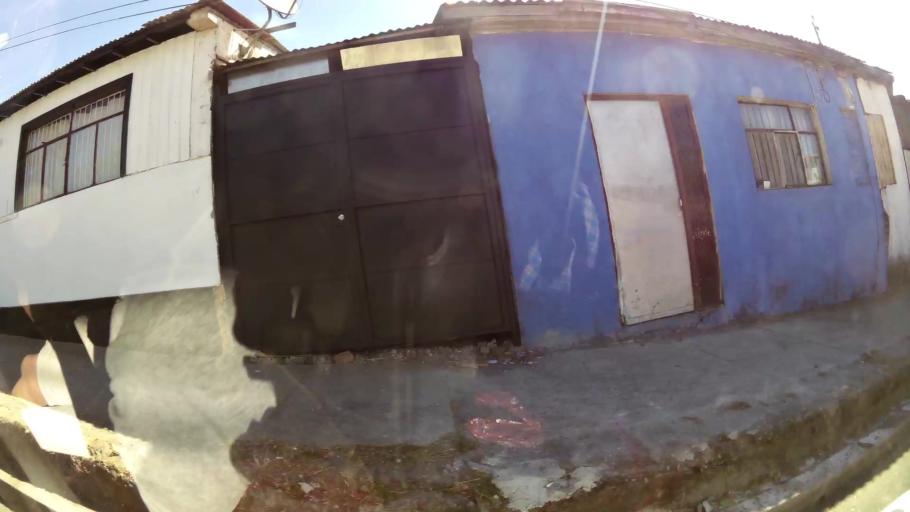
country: CL
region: Biobio
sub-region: Provincia de Concepcion
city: Penco
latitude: -36.7420
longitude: -72.9963
